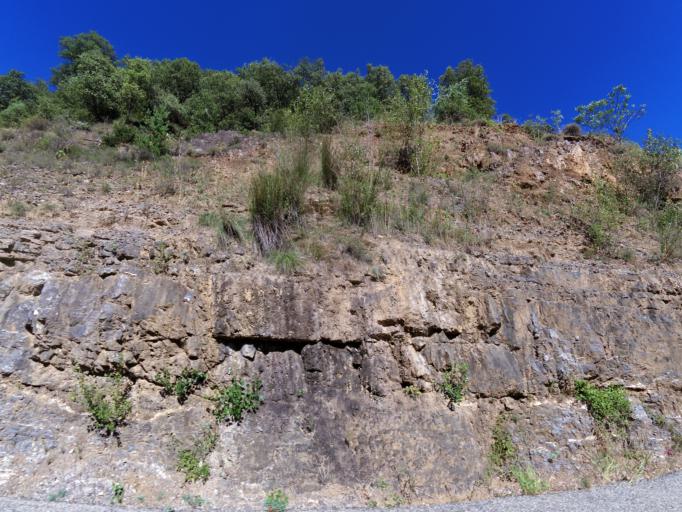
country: FR
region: Languedoc-Roussillon
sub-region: Departement du Gard
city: Saint-Jean-du-Gard
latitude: 44.0945
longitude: 3.9189
